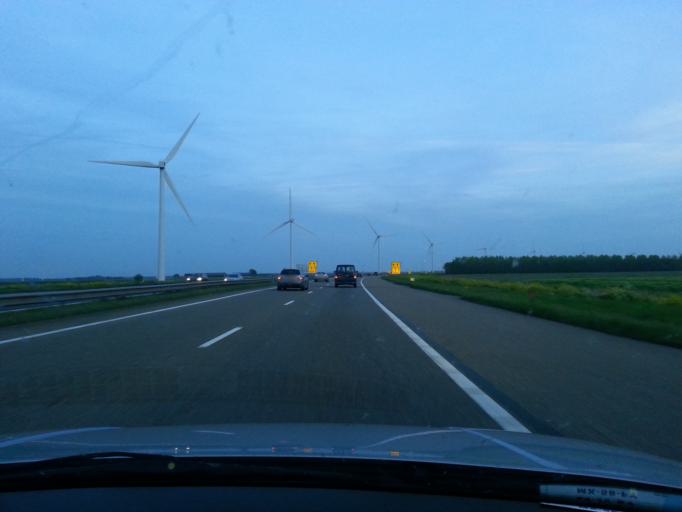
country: NL
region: Utrecht
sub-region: Gemeente Bunschoten
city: Spakenburg
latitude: 52.3444
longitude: 5.3431
